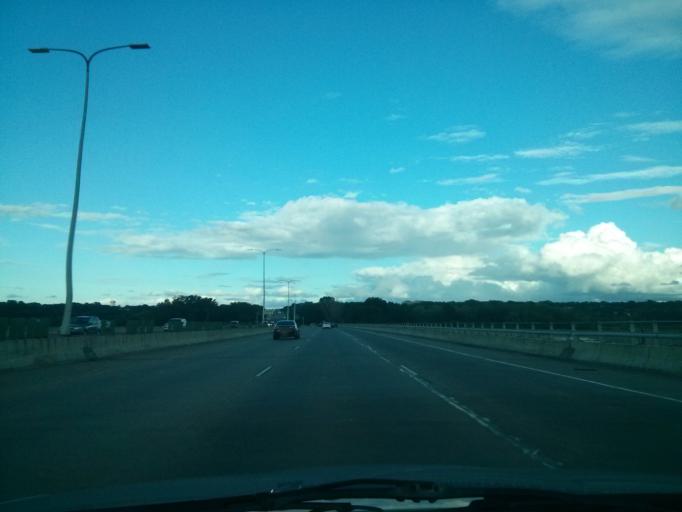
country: US
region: Minnesota
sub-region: Dakota County
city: Mendota Heights
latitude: 44.8615
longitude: -93.1942
